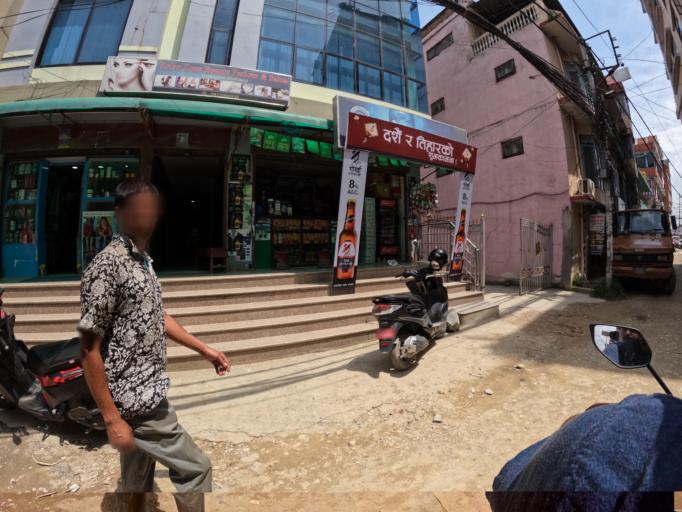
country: NP
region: Central Region
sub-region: Bagmati Zone
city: Patan
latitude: 27.6745
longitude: 85.3716
